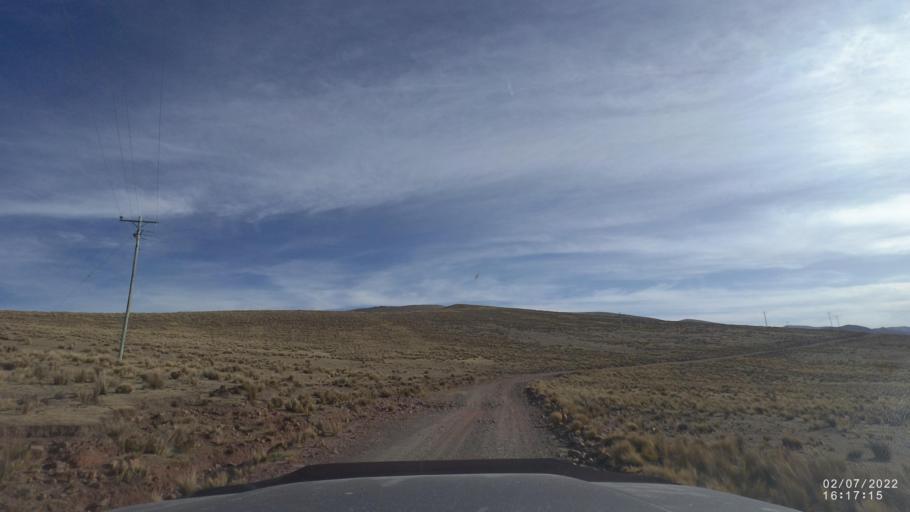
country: BO
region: Cochabamba
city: Irpa Irpa
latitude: -17.9251
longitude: -66.4360
